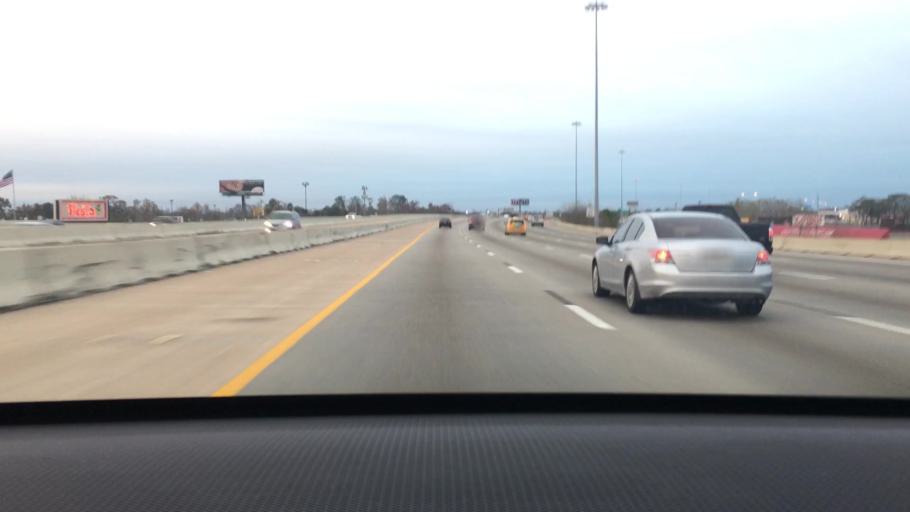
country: US
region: Texas
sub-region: Harris County
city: Aldine
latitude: 29.8613
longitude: -95.3333
